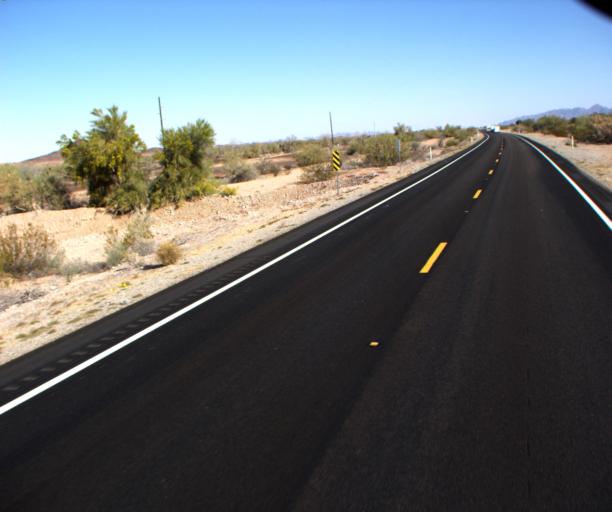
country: US
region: Arizona
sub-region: Yuma County
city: Wellton
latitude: 32.9666
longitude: -114.2915
